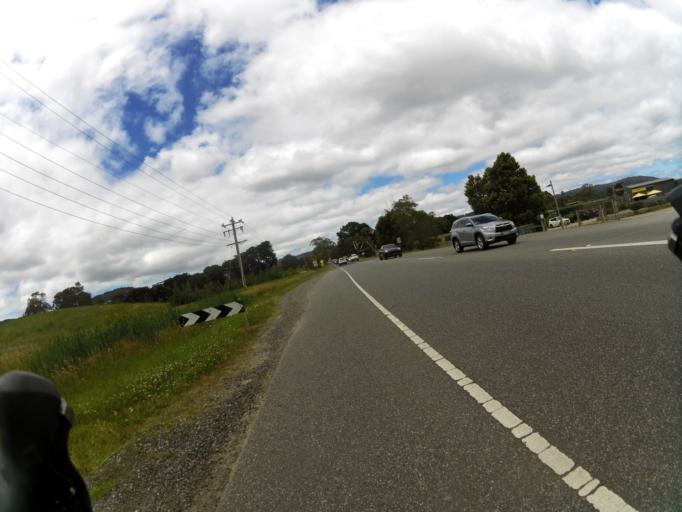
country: AU
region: Victoria
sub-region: Mornington Peninsula
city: Safety Beach
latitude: -38.3324
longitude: 145.0088
